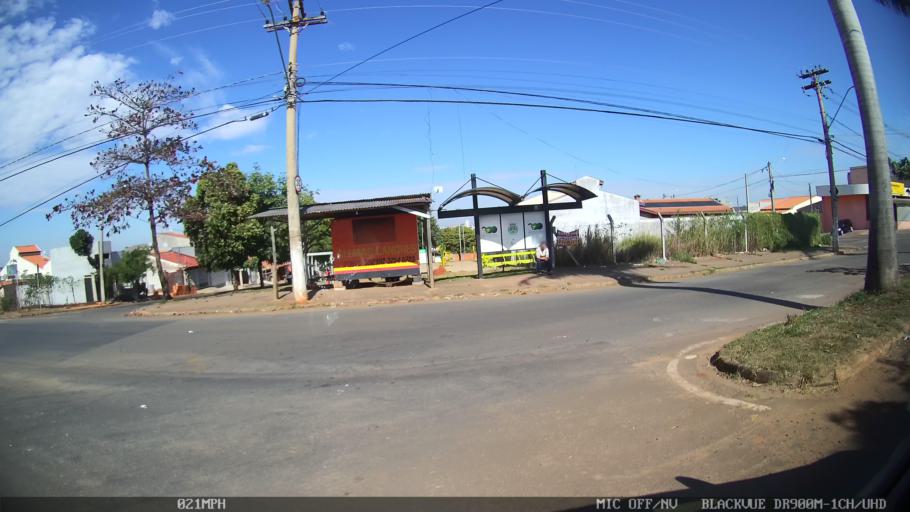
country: BR
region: Sao Paulo
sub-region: Santa Barbara D'Oeste
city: Santa Barbara d'Oeste
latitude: -22.7269
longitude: -47.4028
